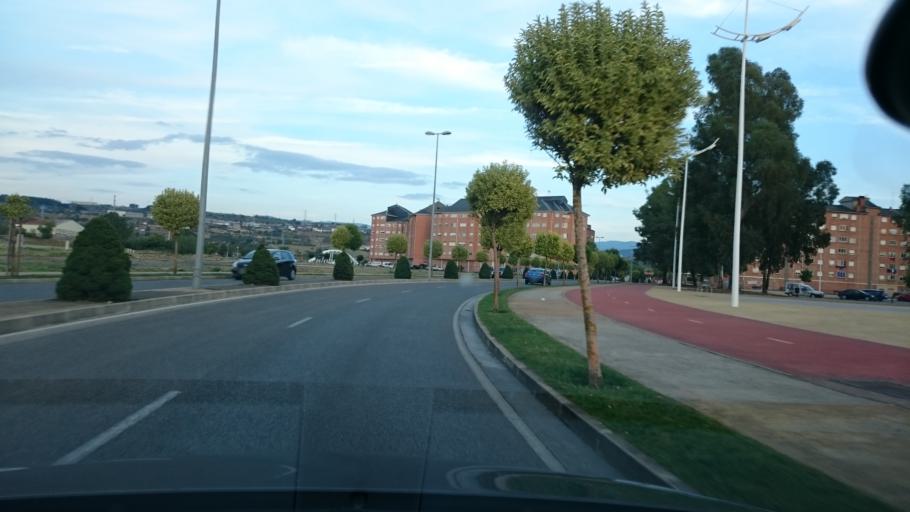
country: ES
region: Castille and Leon
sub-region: Provincia de Leon
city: Ponferrada
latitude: 42.5568
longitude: -6.5975
